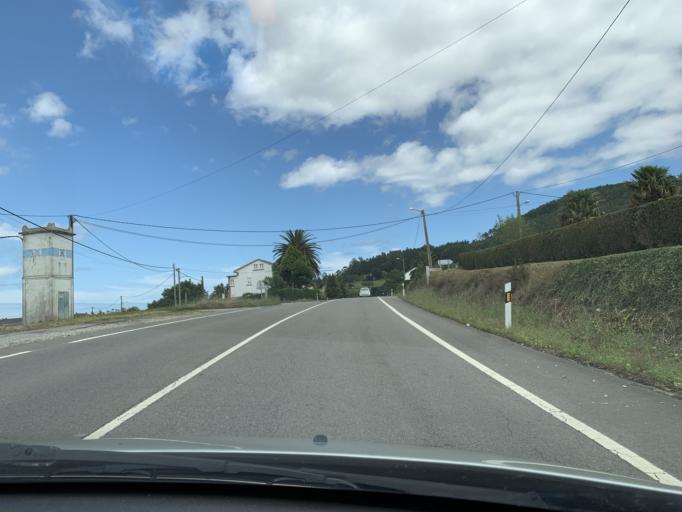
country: ES
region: Galicia
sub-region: Provincia de Lugo
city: Barreiros
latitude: 43.5196
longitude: -7.2713
